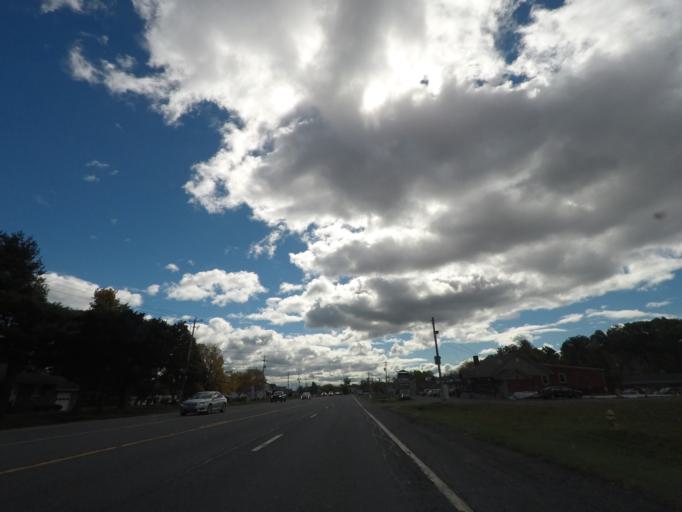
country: US
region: New York
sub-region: Saratoga County
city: Country Knolls
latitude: 42.8530
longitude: -73.7575
